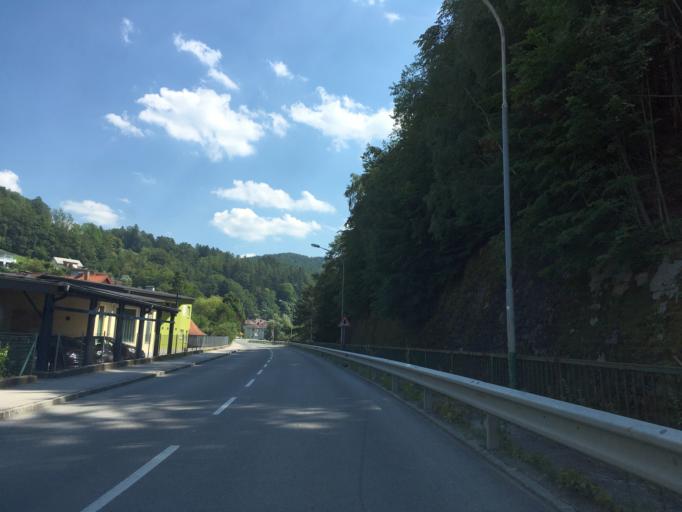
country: AT
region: Lower Austria
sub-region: Politischer Bezirk Neunkirchen
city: Edlitz
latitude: 47.5967
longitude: 16.1407
